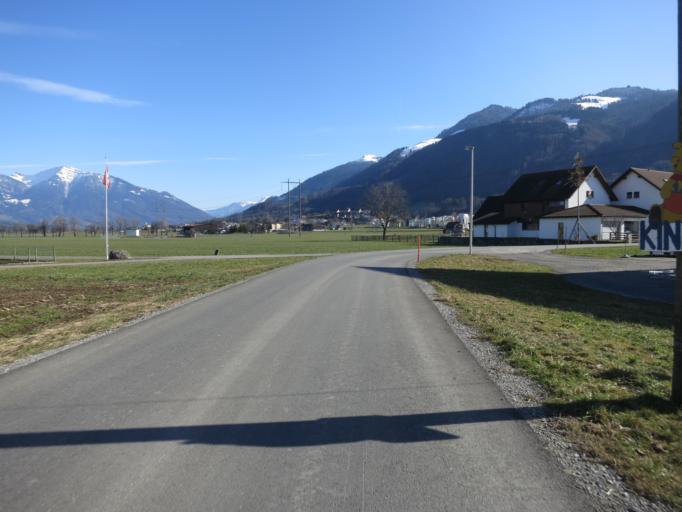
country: CH
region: Schwyz
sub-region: Bezirk March
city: Schubelbach
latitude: 47.1798
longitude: 8.9274
